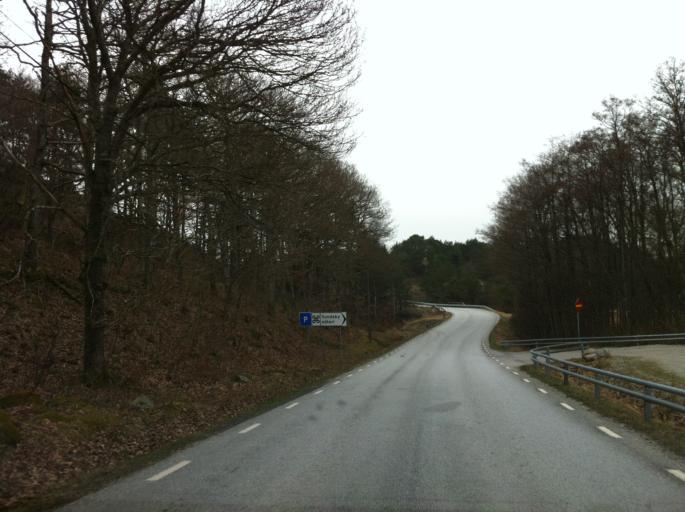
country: SE
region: Vaestra Goetaland
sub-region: Orust
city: Henan
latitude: 58.2609
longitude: 11.6788
